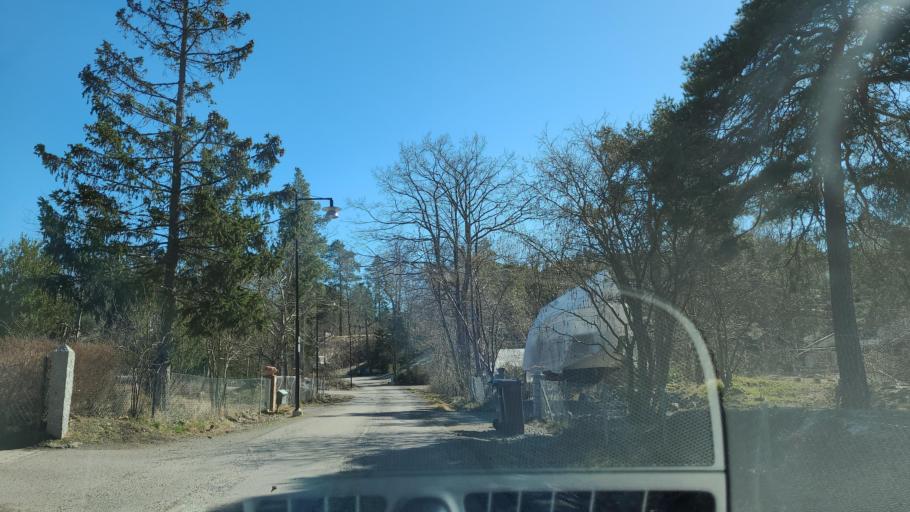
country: SE
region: Stockholm
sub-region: Lidingo
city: Brevik
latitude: 59.3291
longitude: 18.2234
